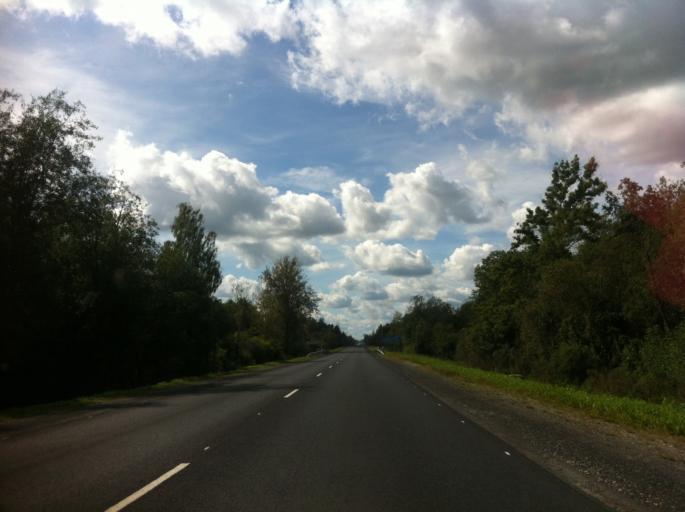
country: RU
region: Pskov
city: Izborsk
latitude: 57.7530
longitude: 28.0594
